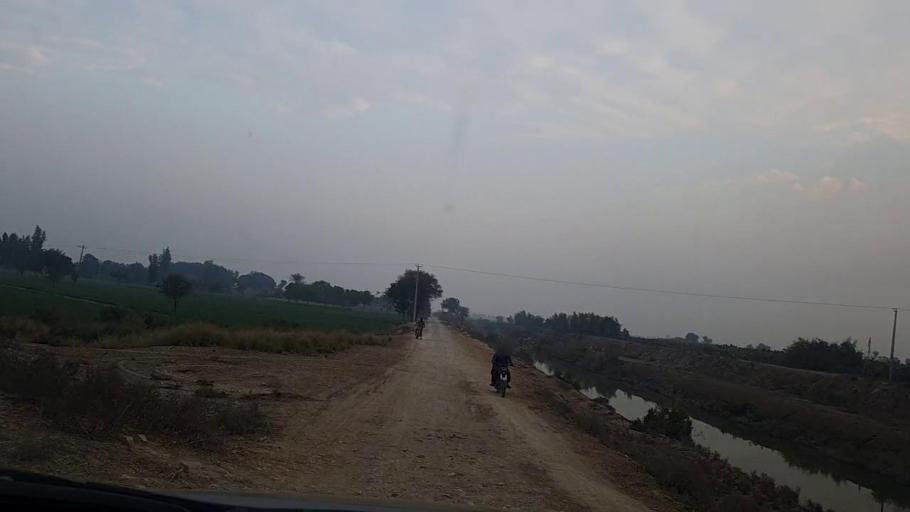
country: PK
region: Sindh
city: Sakrand
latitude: 26.2888
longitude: 68.2373
